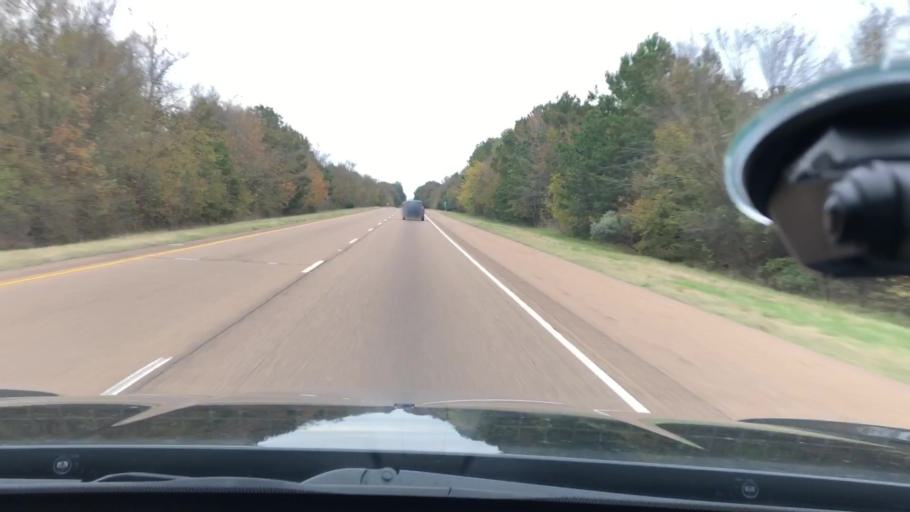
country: US
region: Arkansas
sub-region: Nevada County
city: Prescott
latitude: 33.7810
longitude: -93.4634
